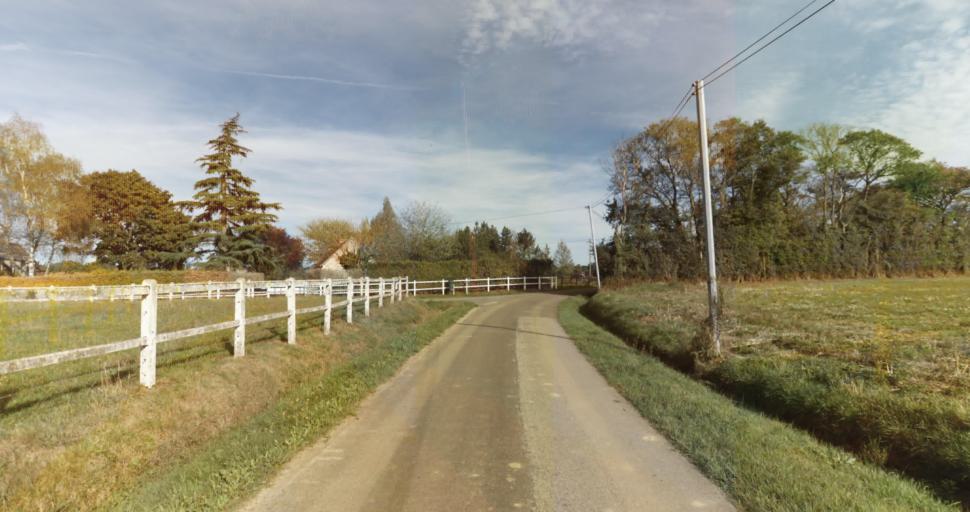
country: FR
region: Lower Normandy
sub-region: Departement de l'Orne
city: Gace
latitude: 48.7128
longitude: 0.2684
